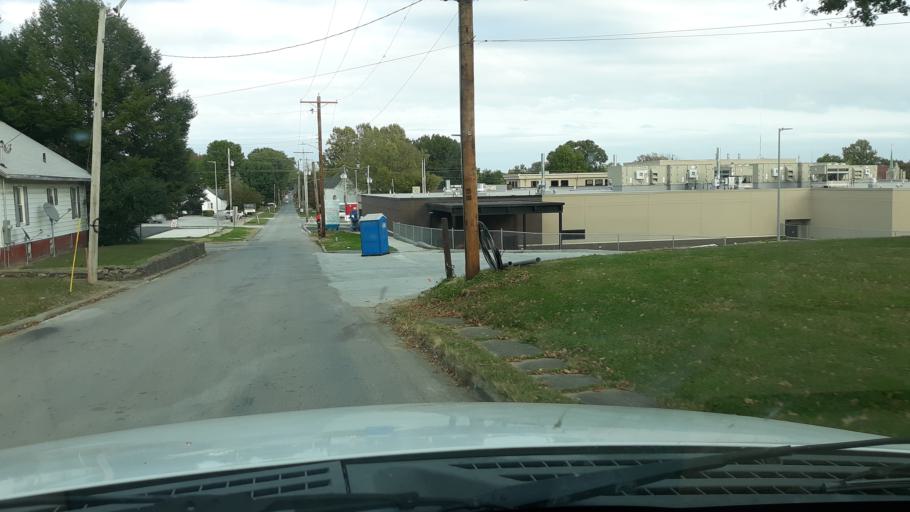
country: US
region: Illinois
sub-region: Saline County
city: Eldorado
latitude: 37.8162
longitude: -88.4438
